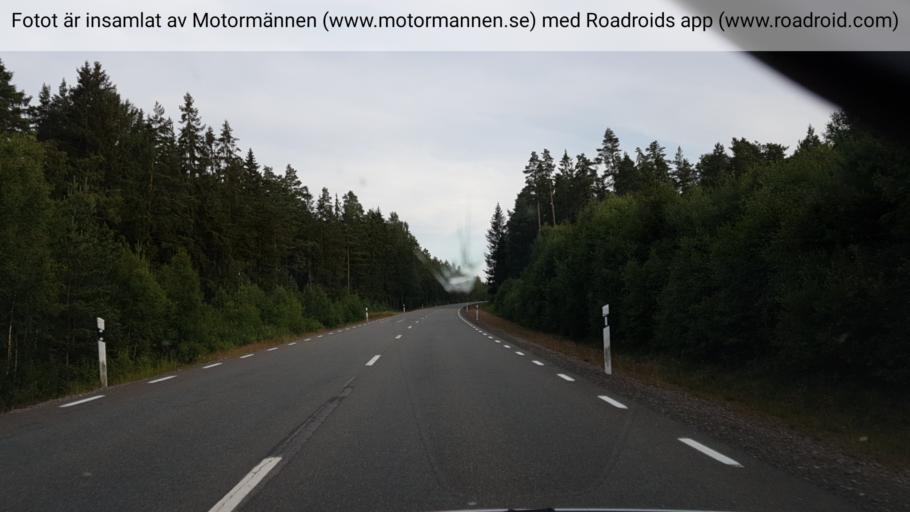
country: SE
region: Vaestra Goetaland
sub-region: Tibro Kommun
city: Tibro
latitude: 58.5439
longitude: 14.1466
